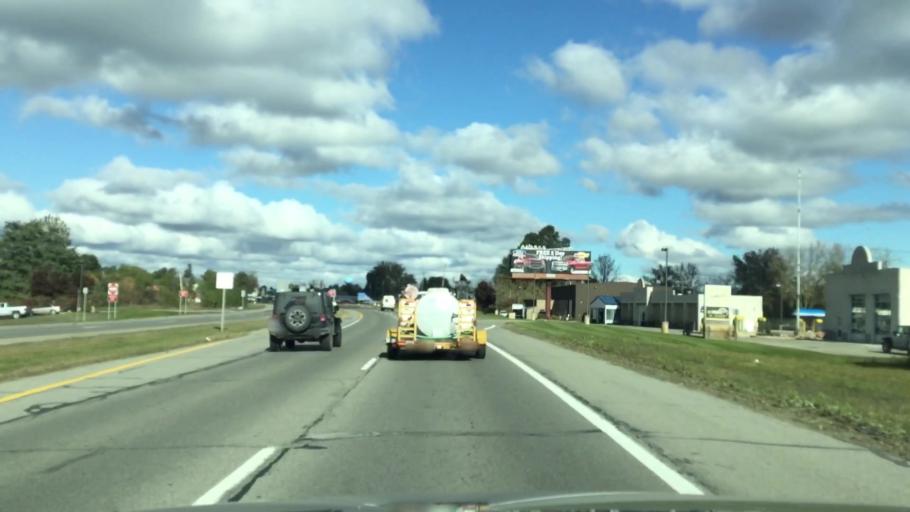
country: US
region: Michigan
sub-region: Oakland County
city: Lake Orion
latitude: 42.8056
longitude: -83.2481
